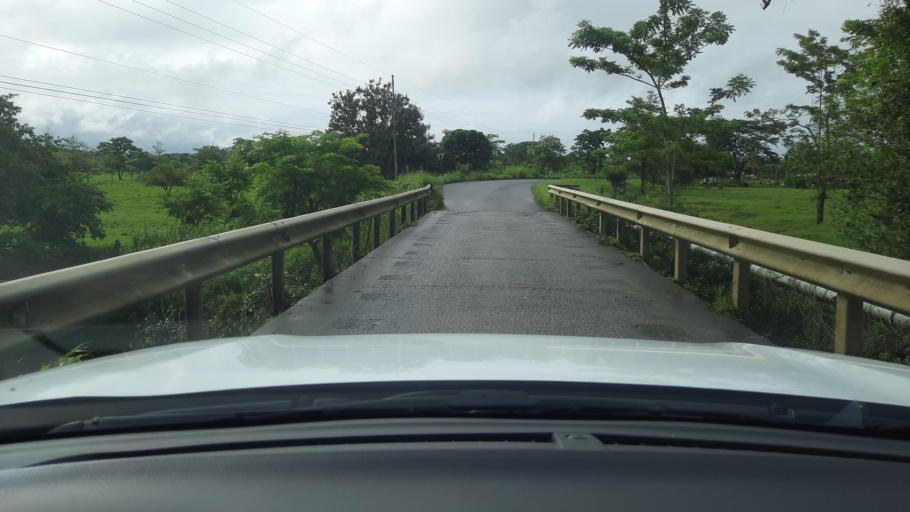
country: CR
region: Alajuela
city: San Jose
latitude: 10.9339
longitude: -85.1018
